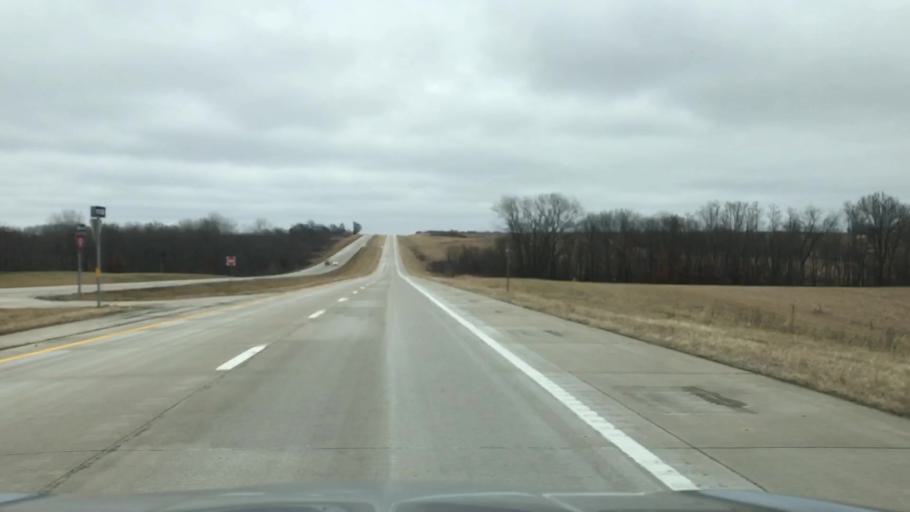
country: US
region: Missouri
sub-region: Livingston County
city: Chillicothe
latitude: 39.7379
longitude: -93.7018
